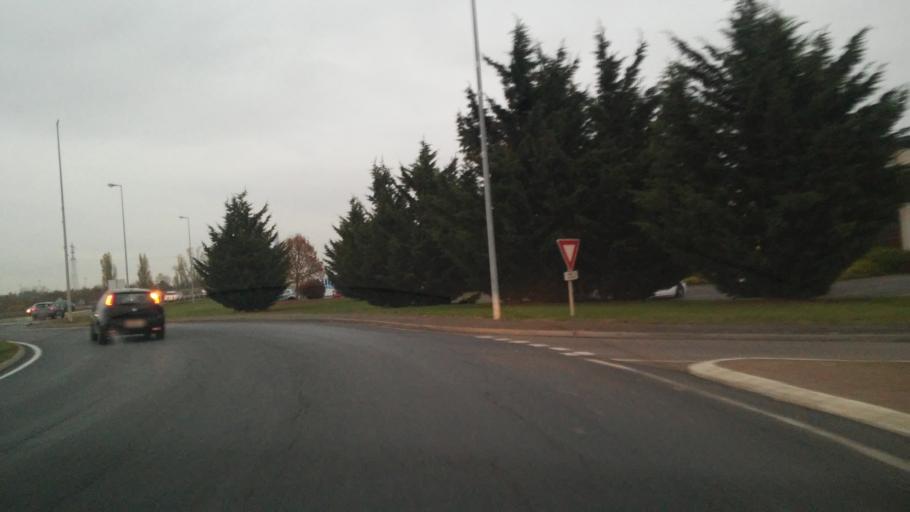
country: FR
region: Lorraine
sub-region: Departement de la Moselle
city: Talange
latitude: 49.2407
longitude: 6.1758
